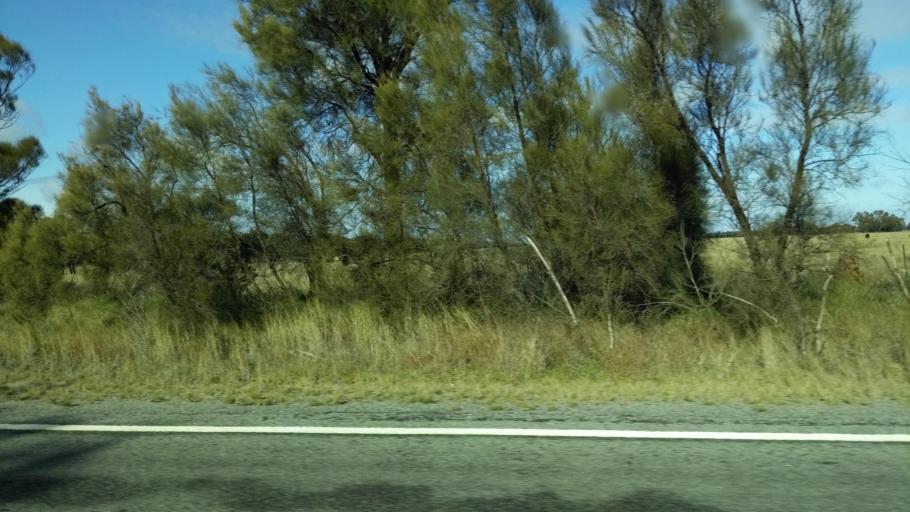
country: AU
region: New South Wales
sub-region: Narrandera
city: Narrandera
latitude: -34.7557
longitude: 146.8609
